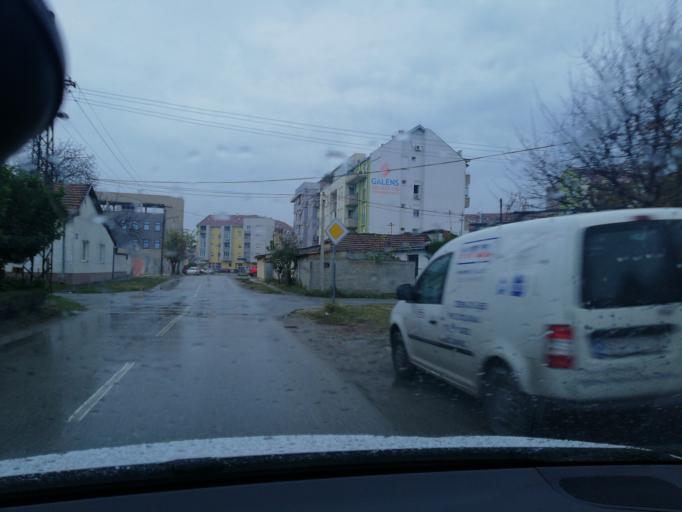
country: RS
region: Autonomna Pokrajina Vojvodina
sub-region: Juznobacki Okrug
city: Novi Sad
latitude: 45.2428
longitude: 19.8025
